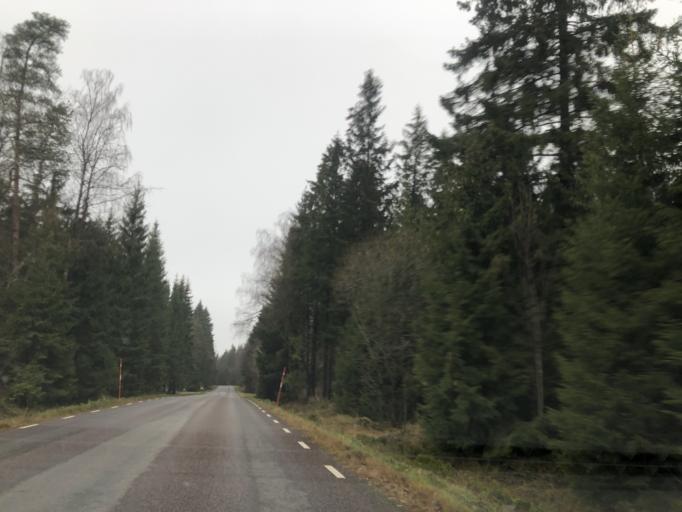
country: SE
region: Vaestra Goetaland
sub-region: Ulricehamns Kommun
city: Ulricehamn
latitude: 57.7598
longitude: 13.4904
